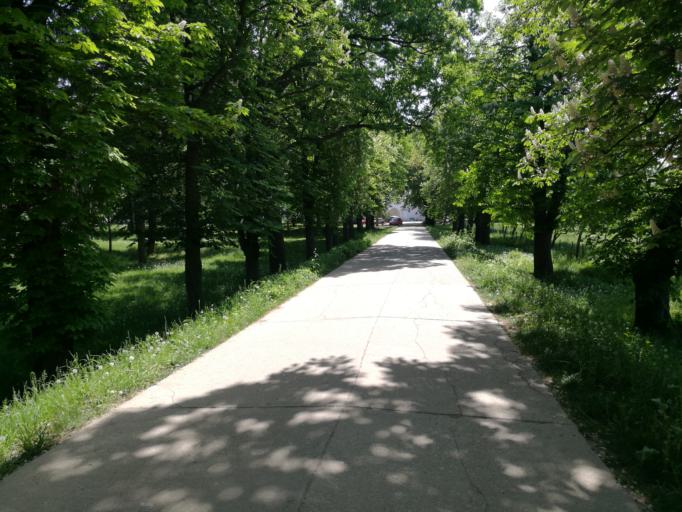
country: RO
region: Ilfov
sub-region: Comuna Gradistea
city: Gradistea
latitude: 44.6767
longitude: 26.2654
